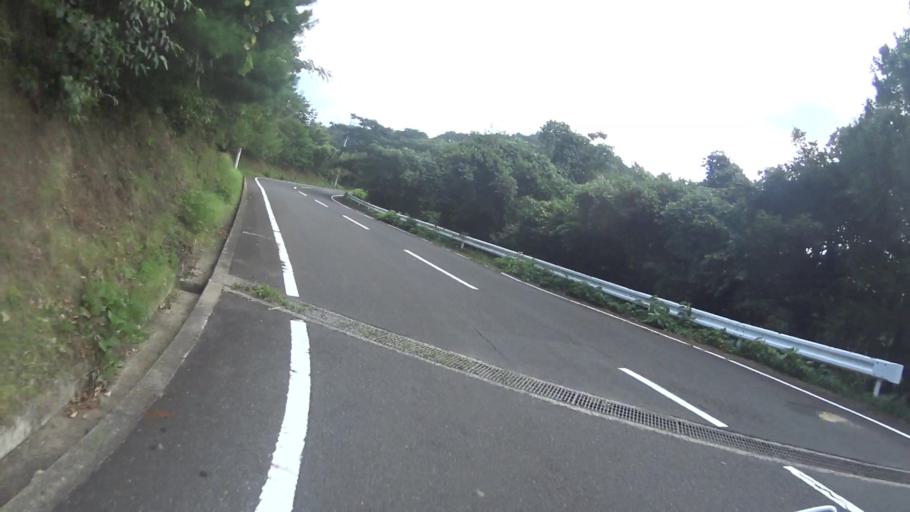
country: JP
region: Kyoto
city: Miyazu
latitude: 35.7393
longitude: 135.1749
